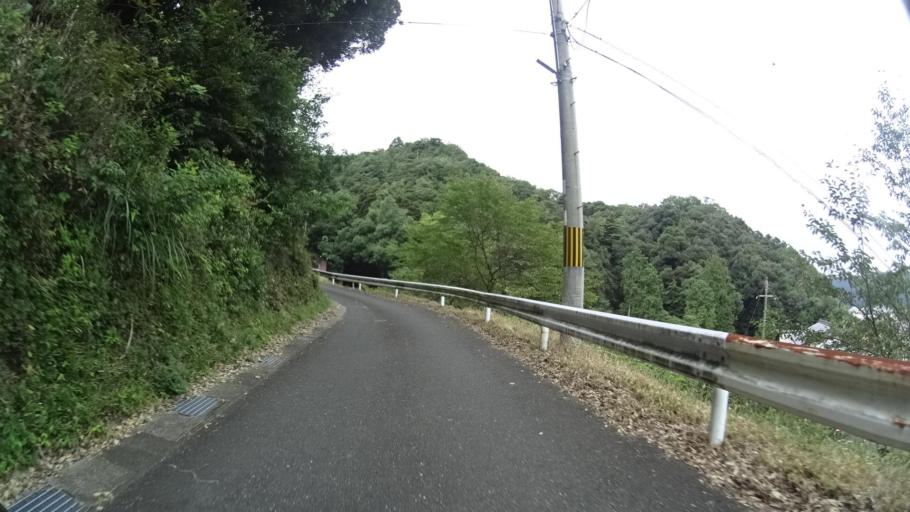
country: JP
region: Kyoto
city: Miyazu
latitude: 35.5274
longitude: 135.1841
